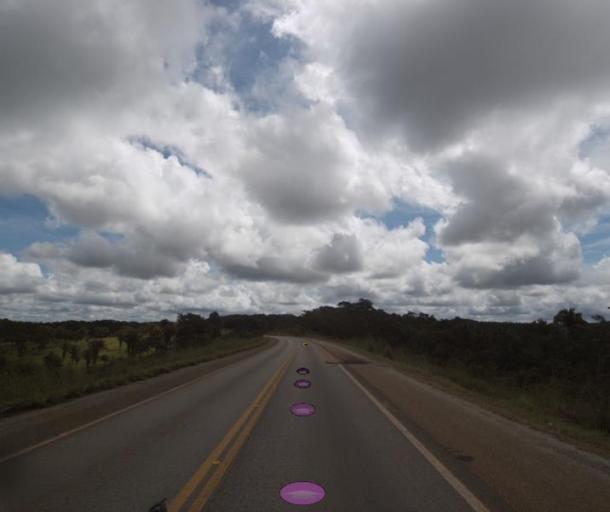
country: BR
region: Goias
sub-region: Pirenopolis
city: Pirenopolis
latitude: -15.7626
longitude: -48.5726
